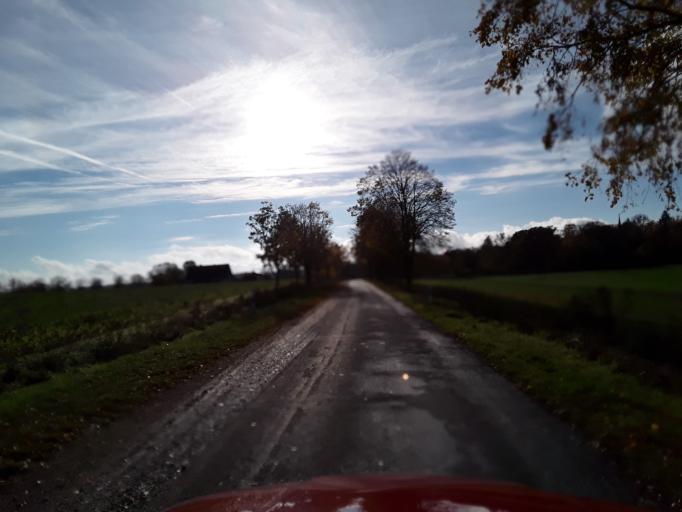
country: DE
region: Brandenburg
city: Mittenwalde
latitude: 53.2747
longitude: 13.6985
